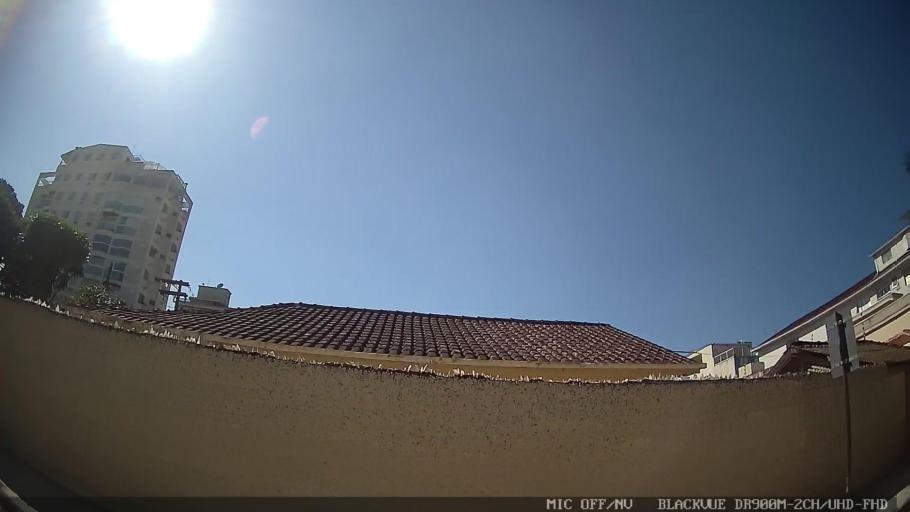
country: BR
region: Sao Paulo
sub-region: Guaruja
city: Guaruja
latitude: -23.9854
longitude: -46.2045
